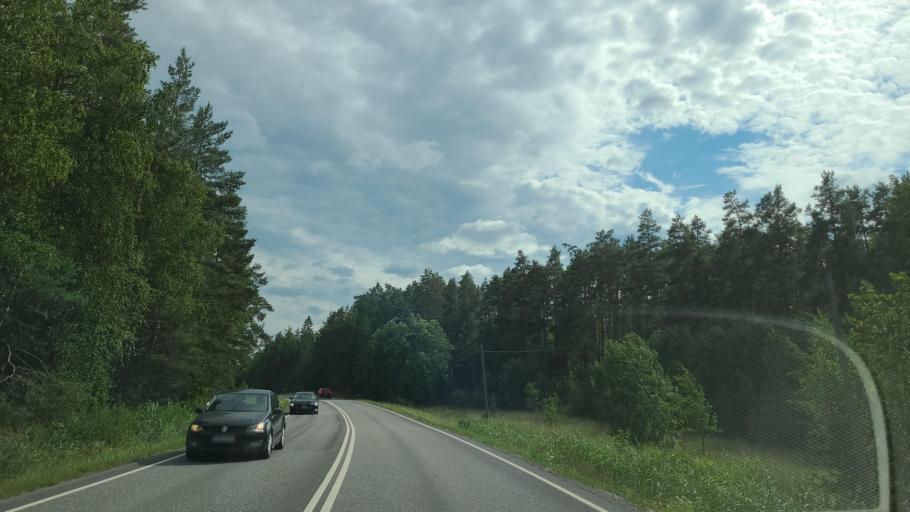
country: FI
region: Varsinais-Suomi
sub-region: Turku
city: Merimasku
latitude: 60.4462
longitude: 21.8972
